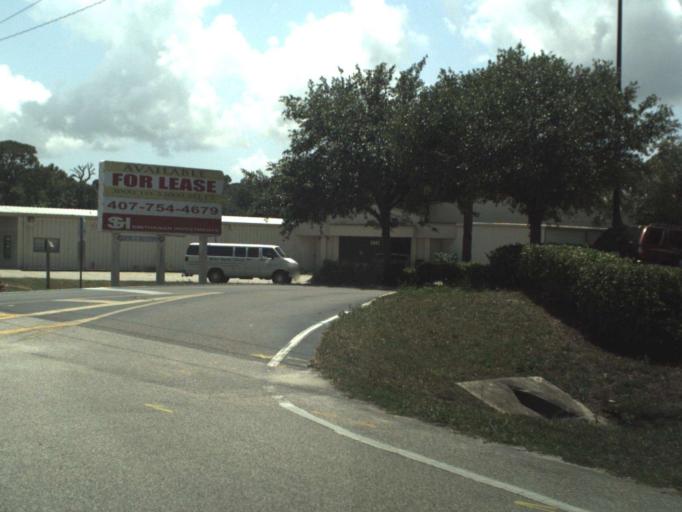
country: US
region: Florida
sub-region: Volusia County
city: Edgewater
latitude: 28.9474
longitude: -80.8838
